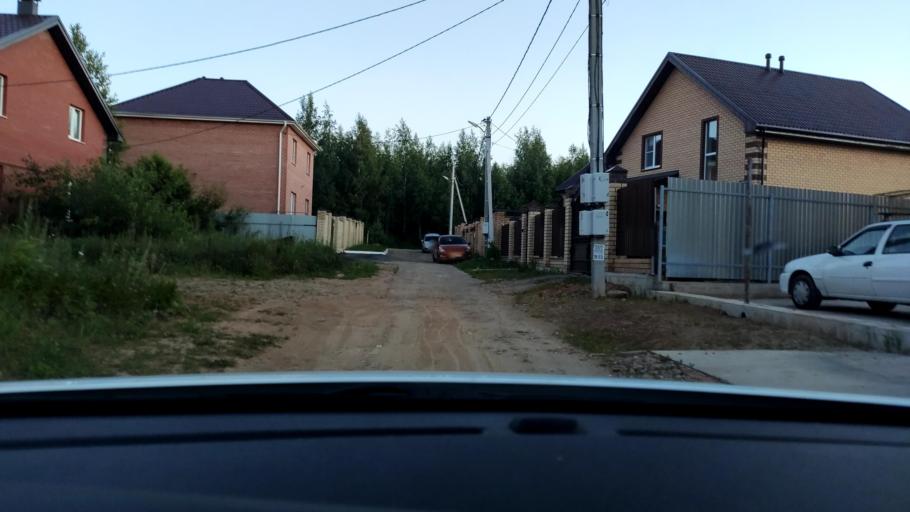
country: RU
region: Tatarstan
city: Stolbishchi
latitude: 55.7351
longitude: 49.2668
